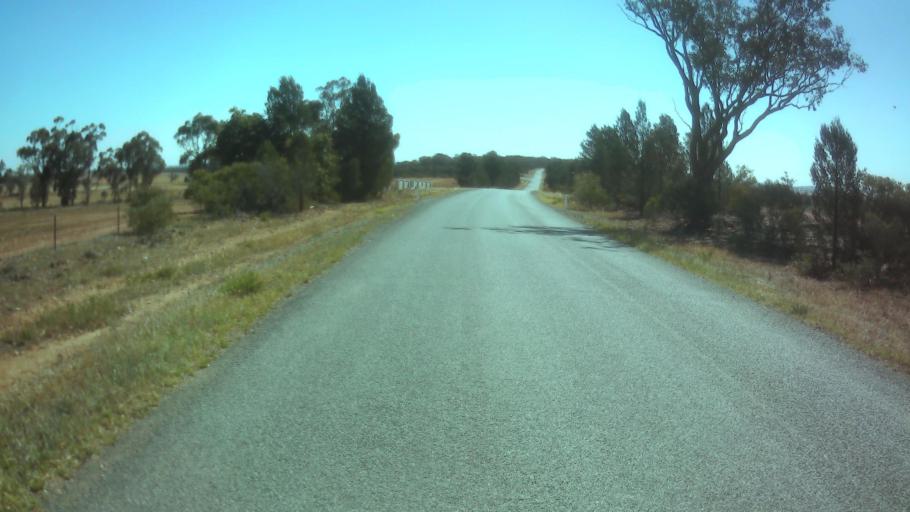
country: AU
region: New South Wales
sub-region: Weddin
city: Grenfell
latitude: -33.7543
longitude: 147.8363
